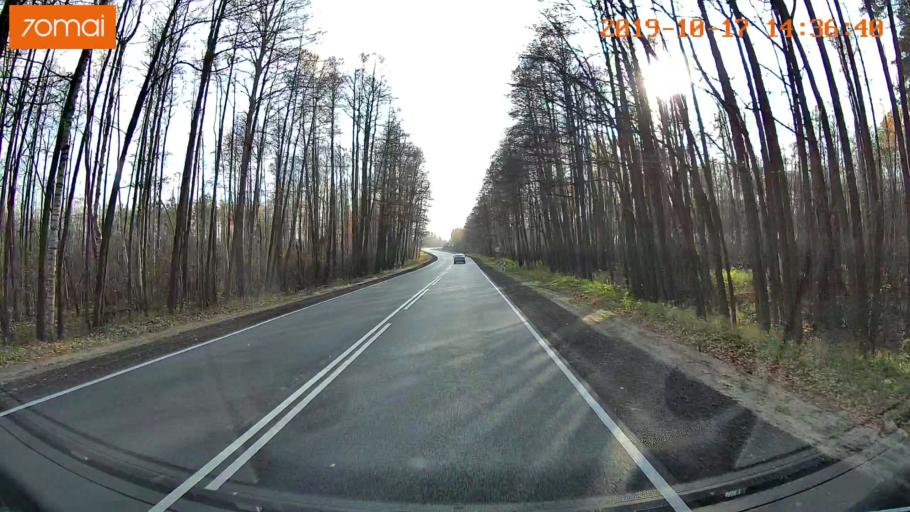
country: RU
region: Rjazan
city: Solotcha
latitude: 54.8881
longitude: 40.0018
